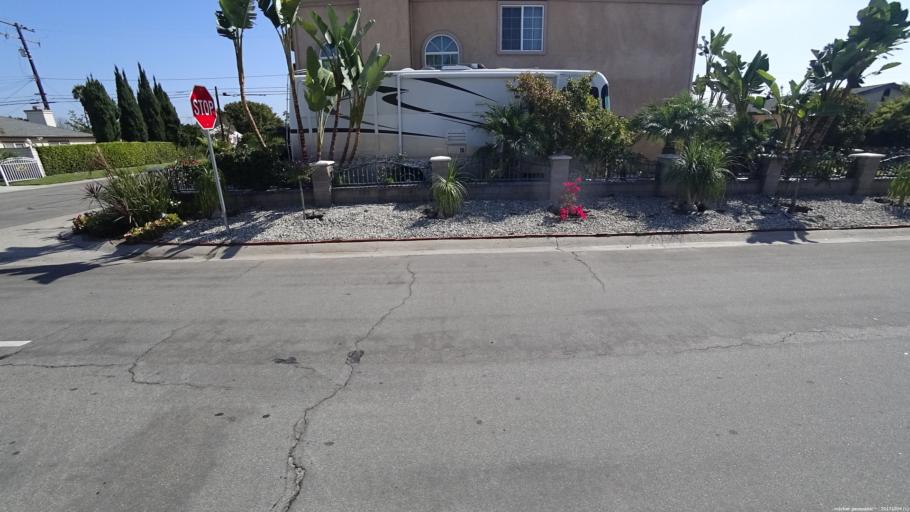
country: US
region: California
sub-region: Orange County
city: Garden Grove
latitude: 33.7921
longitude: -117.9469
